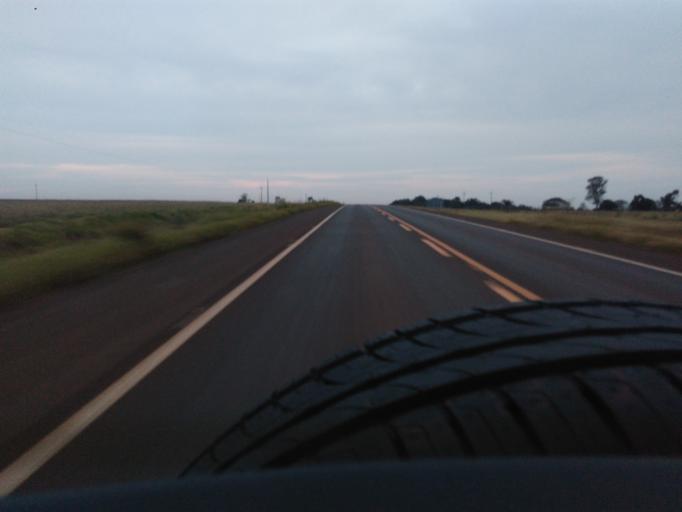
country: BR
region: Mato Grosso do Sul
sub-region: Ponta Pora
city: Ponta Pora
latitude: -22.5214
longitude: -55.4527
